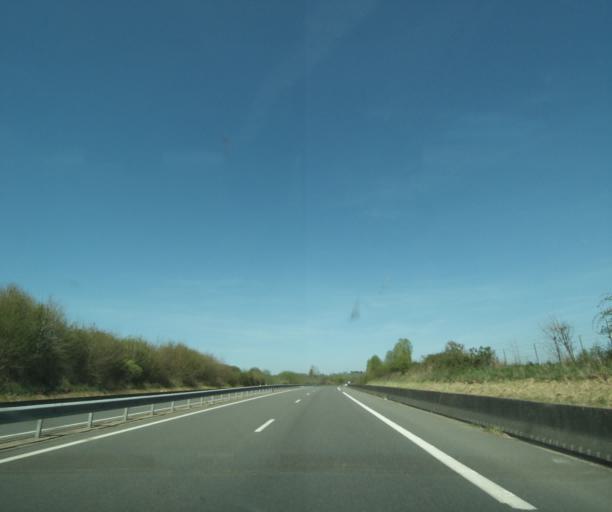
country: FR
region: Bourgogne
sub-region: Departement de la Nievre
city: Pougues-les-Eaux
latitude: 47.0643
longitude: 3.1298
